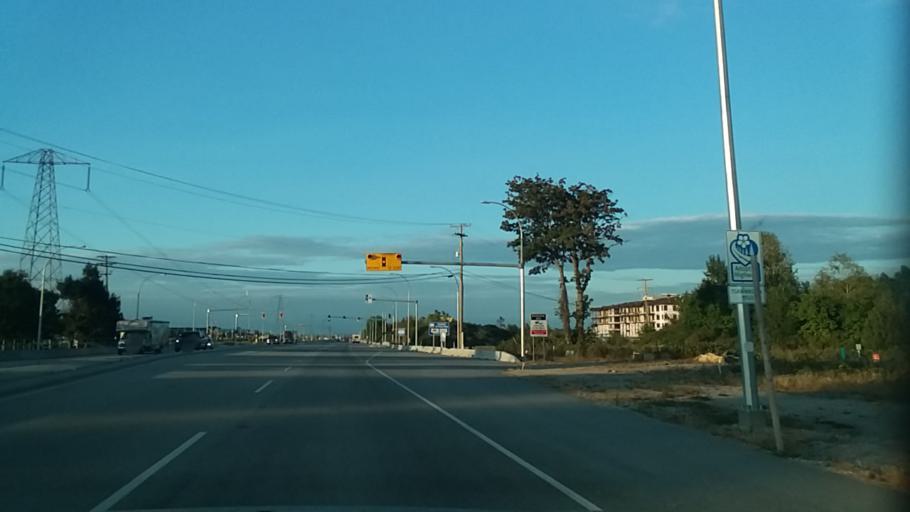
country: US
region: Washington
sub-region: Whatcom County
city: Point Roberts
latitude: 49.0316
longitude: -123.0919
